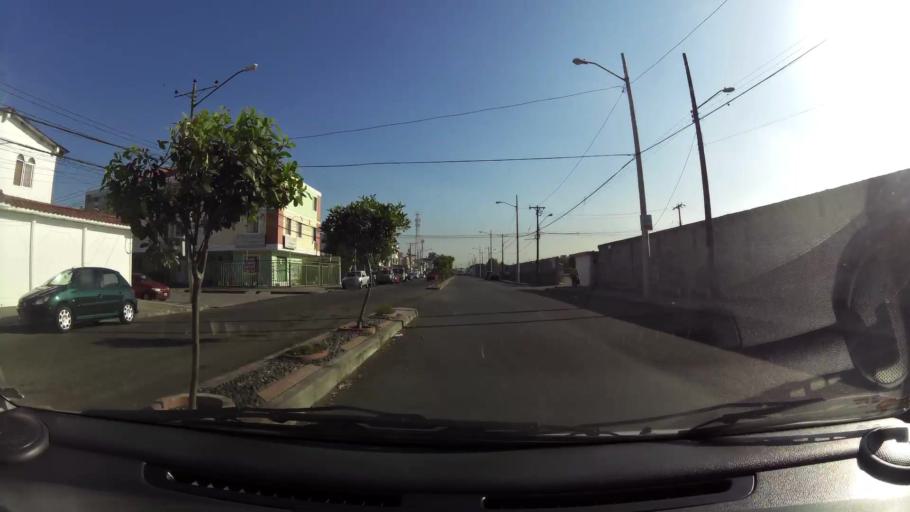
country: EC
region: Guayas
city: Eloy Alfaro
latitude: -2.1698
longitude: -79.8827
